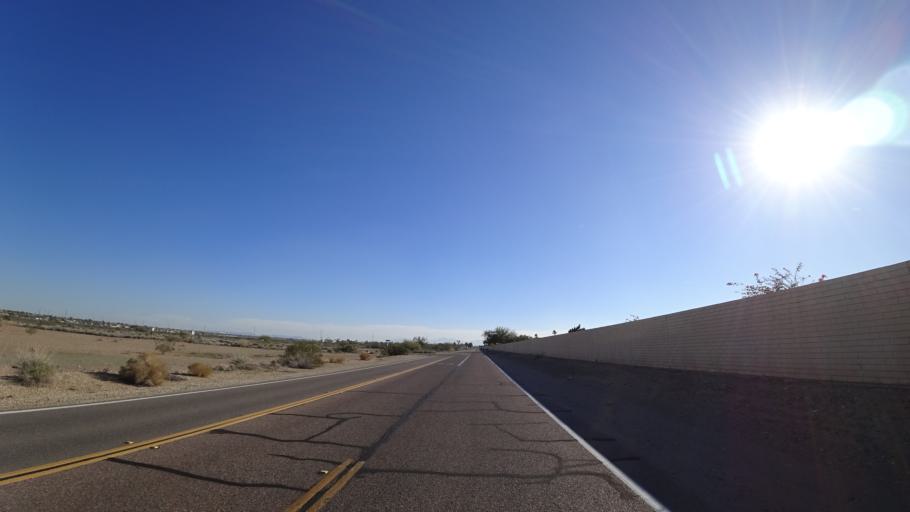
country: US
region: Arizona
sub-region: Maricopa County
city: Surprise
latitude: 33.6471
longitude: -112.3250
